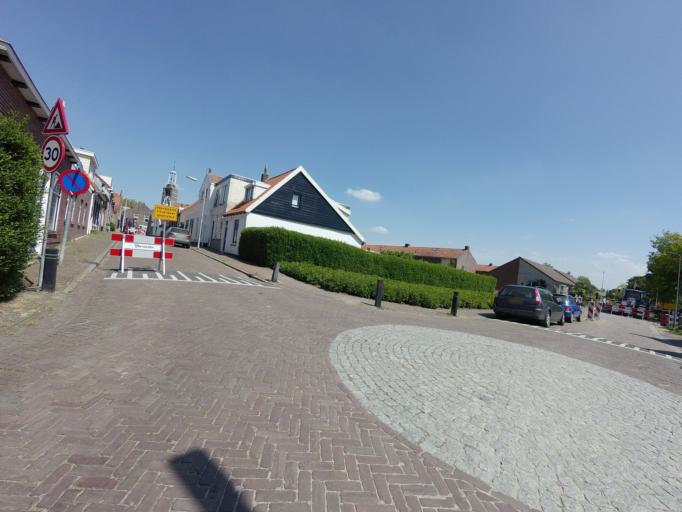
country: NL
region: Zeeland
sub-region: Schouwen-Duiveland
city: Bruinisse
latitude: 51.6249
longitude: 3.9818
